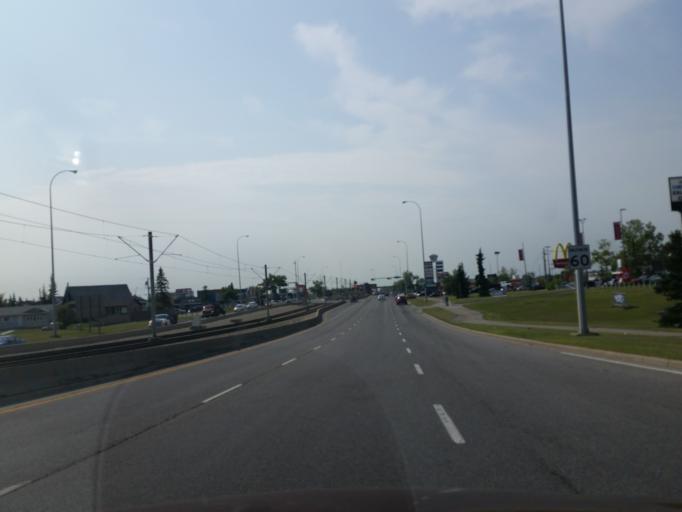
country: CA
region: Alberta
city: Calgary
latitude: 51.0647
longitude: -113.9820
